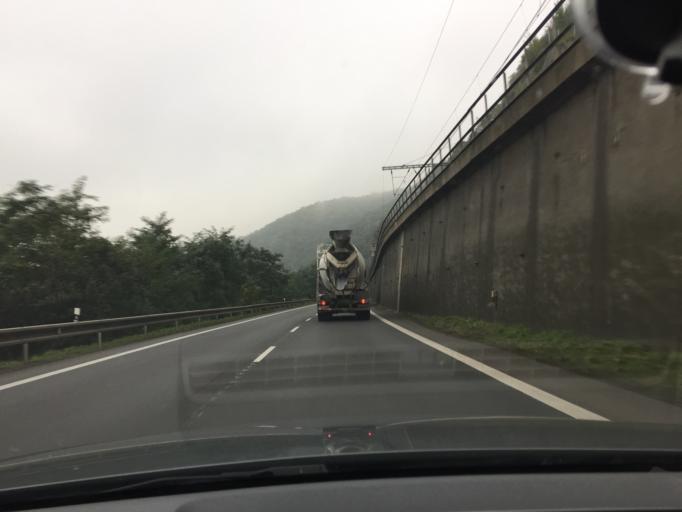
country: CZ
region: Ustecky
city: Lovosice
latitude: 50.5513
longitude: 14.0384
